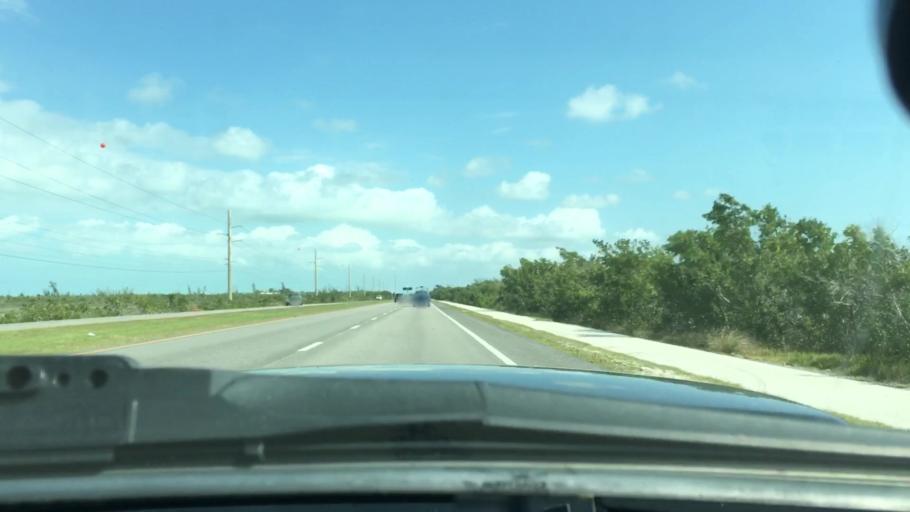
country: US
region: Florida
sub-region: Monroe County
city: Stock Island
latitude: 24.5821
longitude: -81.7032
